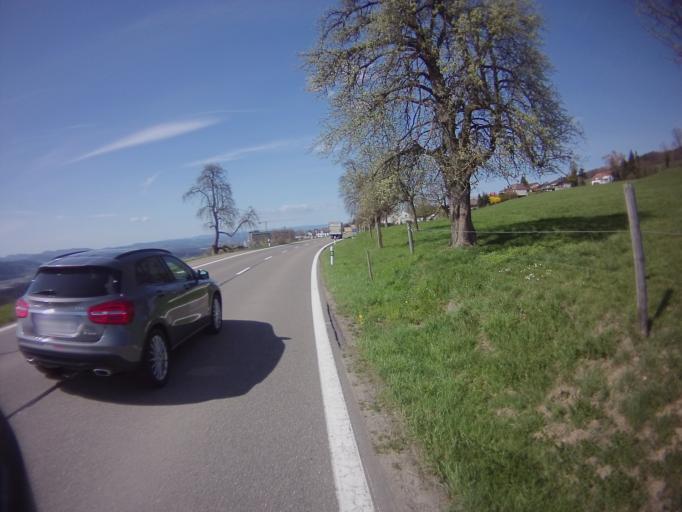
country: CH
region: Aargau
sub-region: Bezirk Baden
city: Kunten
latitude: 47.3826
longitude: 8.3487
